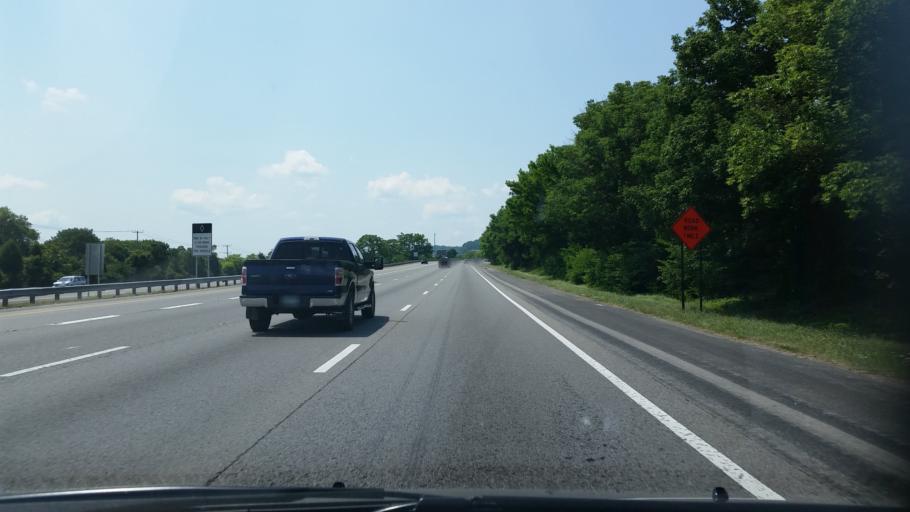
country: US
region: Tennessee
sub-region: Williamson County
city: Brentwood
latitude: 36.0527
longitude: -86.7756
